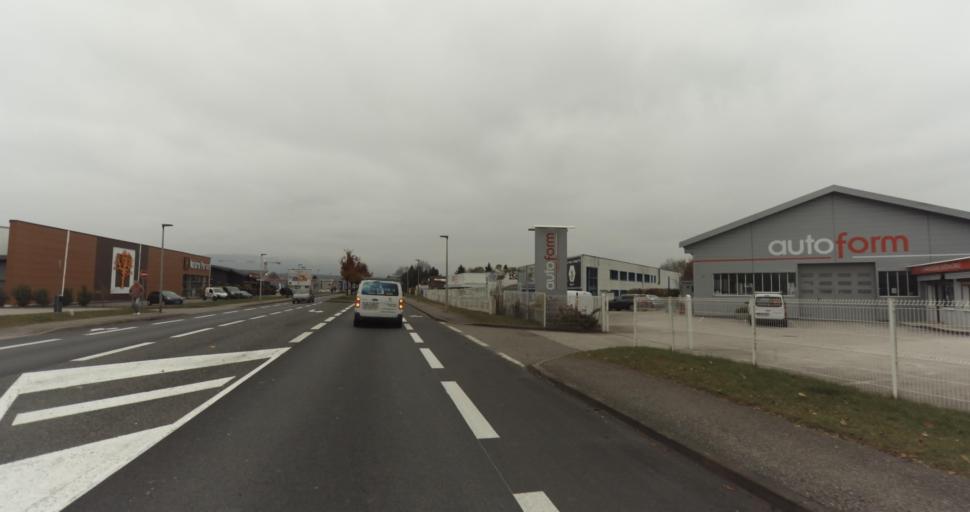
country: FR
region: Rhone-Alpes
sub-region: Departement de la Haute-Savoie
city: Meythet
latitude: 45.9229
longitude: 6.0892
